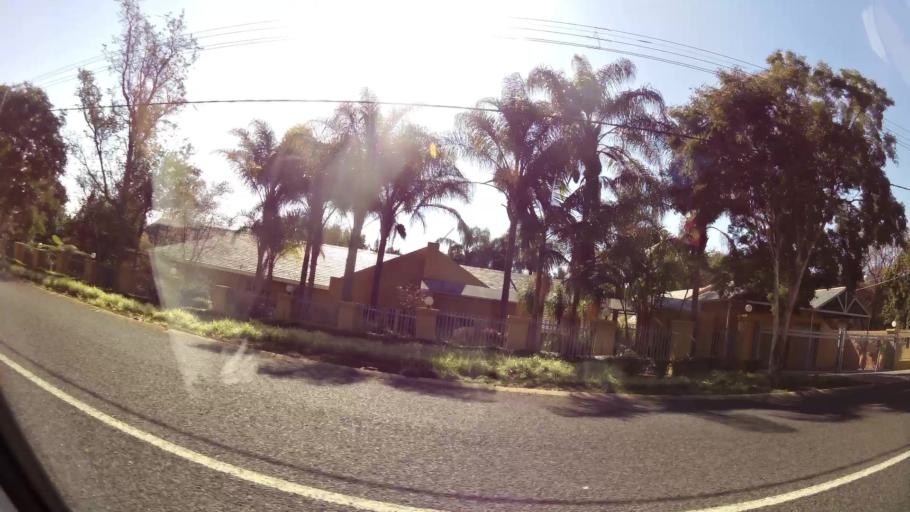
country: ZA
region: Gauteng
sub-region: City of Tshwane Metropolitan Municipality
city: Pretoria
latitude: -25.7570
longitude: 28.2689
